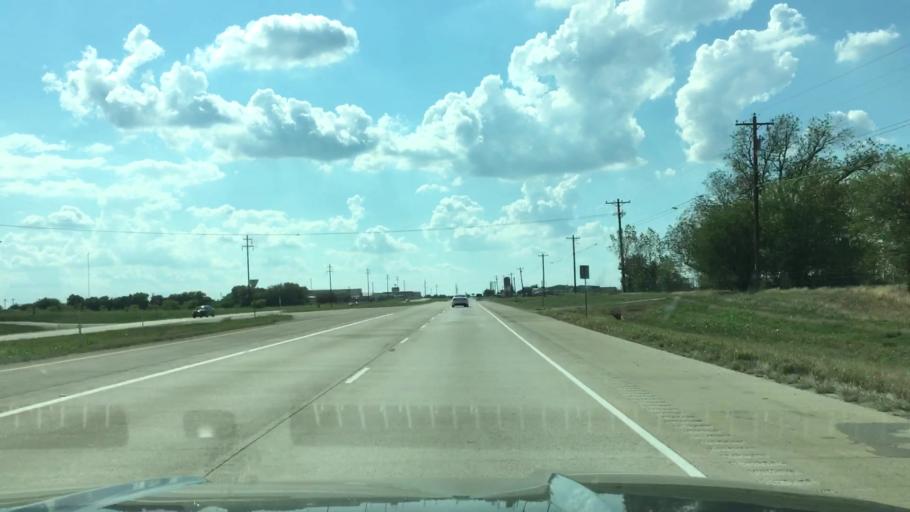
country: US
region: Texas
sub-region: Wise County
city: Rhome
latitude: 33.0371
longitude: -97.4291
